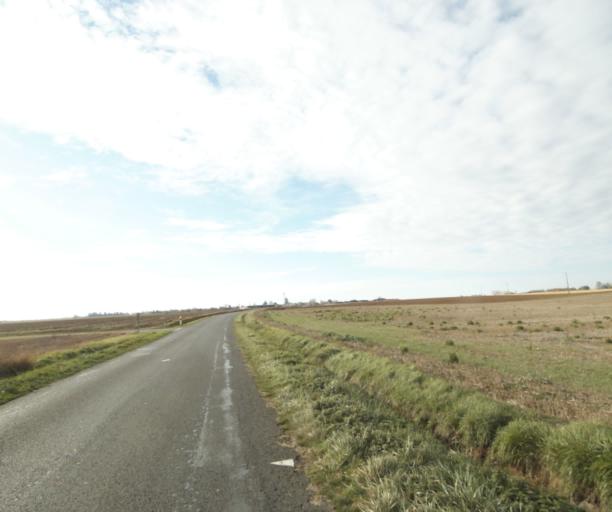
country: FR
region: Poitou-Charentes
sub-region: Departement de la Charente-Maritime
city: Corme-Royal
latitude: 45.7290
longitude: -0.8196
